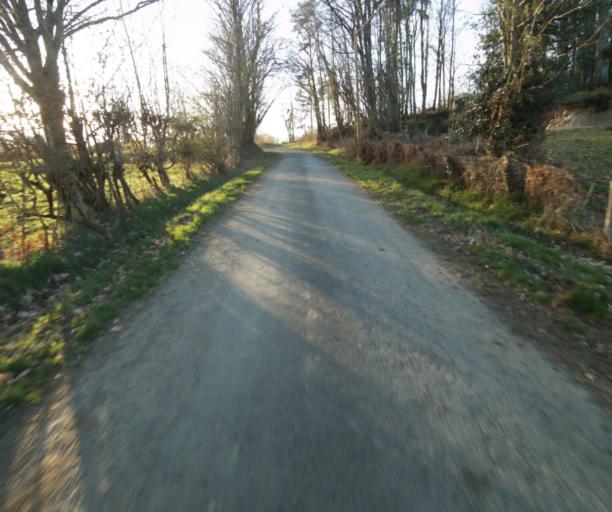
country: FR
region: Limousin
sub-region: Departement de la Correze
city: Uzerche
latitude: 45.3734
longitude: 1.6052
